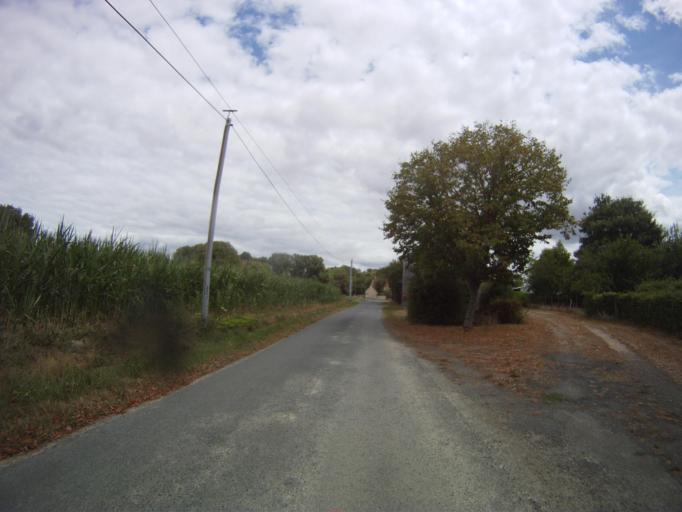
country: FR
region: Centre
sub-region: Departement du Loir-et-Cher
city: Montoire-sur-le-Loir
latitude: 47.6946
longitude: 0.8090
